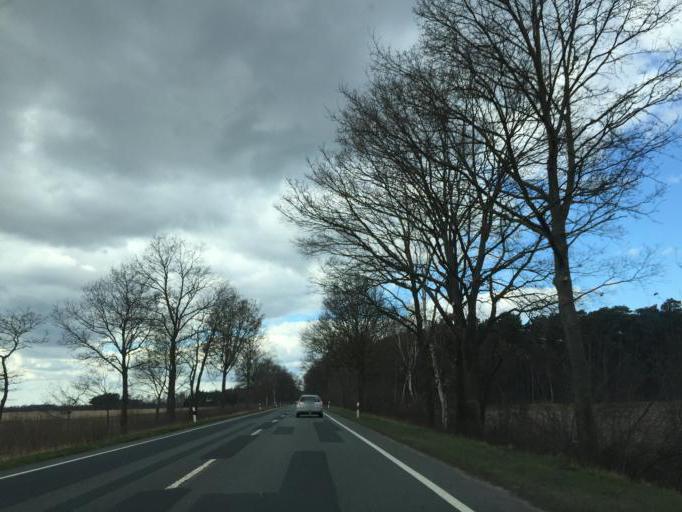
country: DE
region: Lower Saxony
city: Broeckel
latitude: 52.4883
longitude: 10.2487
